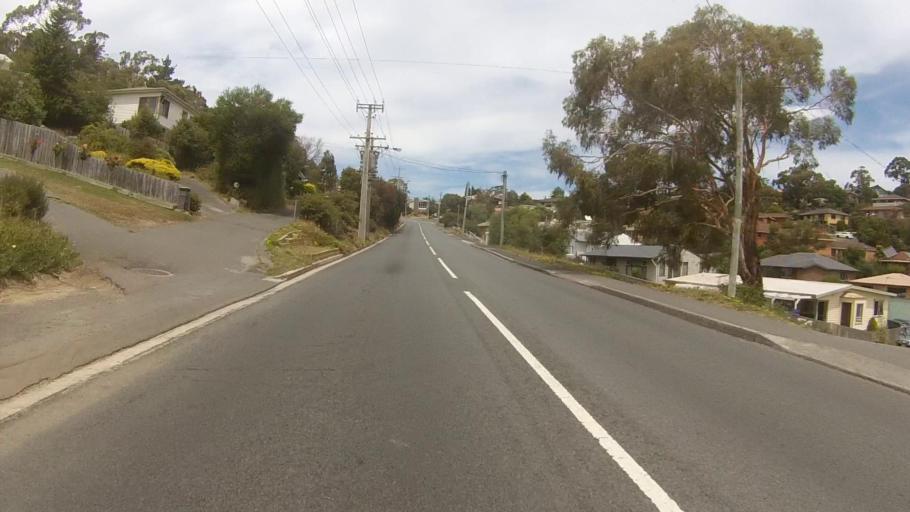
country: AU
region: Tasmania
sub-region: Clarence
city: Lindisfarne
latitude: -42.8533
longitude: 147.3707
